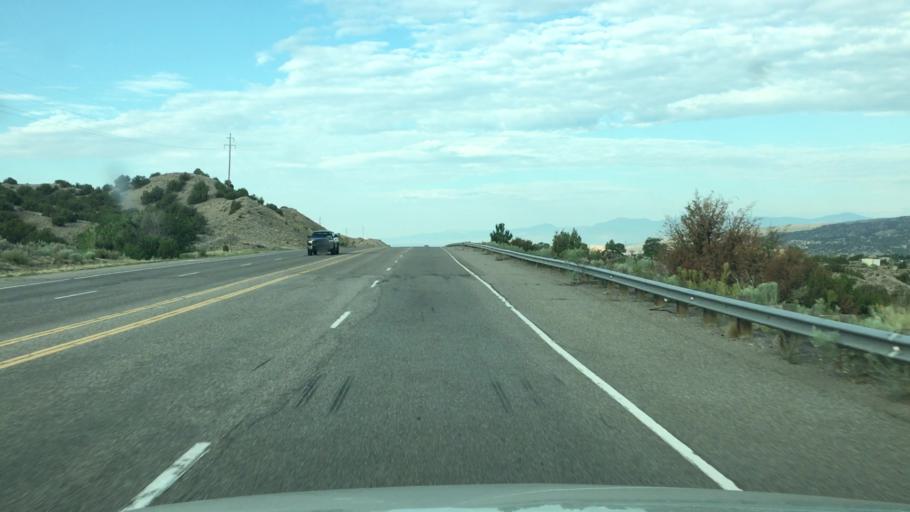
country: US
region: New Mexico
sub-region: Rio Arriba County
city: Ohkay Owingeh
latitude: 36.1496
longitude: -105.9765
